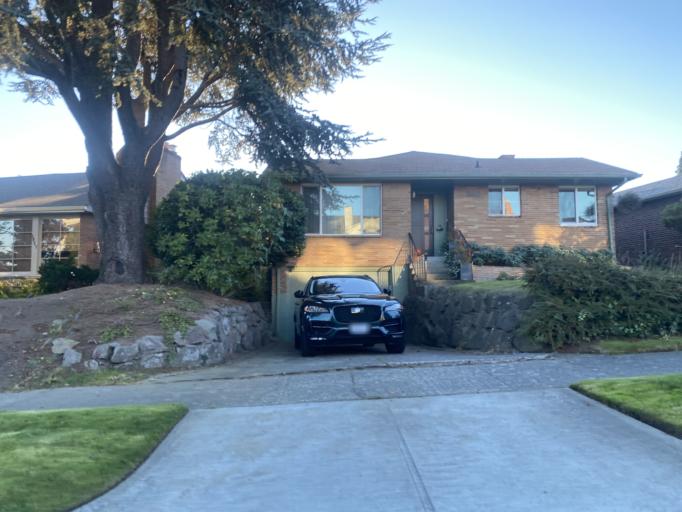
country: US
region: Washington
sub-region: King County
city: Seattle
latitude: 47.6369
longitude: -122.4026
